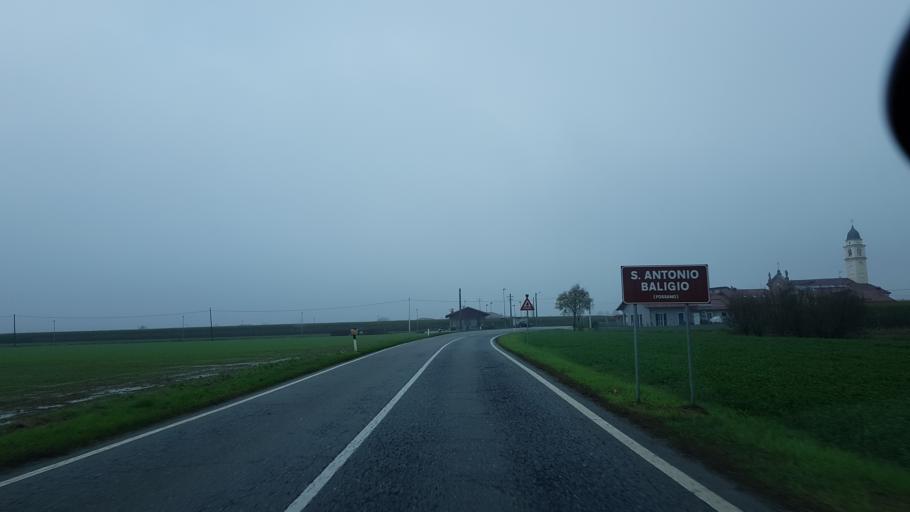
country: IT
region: Piedmont
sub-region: Provincia di Cuneo
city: Genola
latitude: 44.5568
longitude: 7.6591
